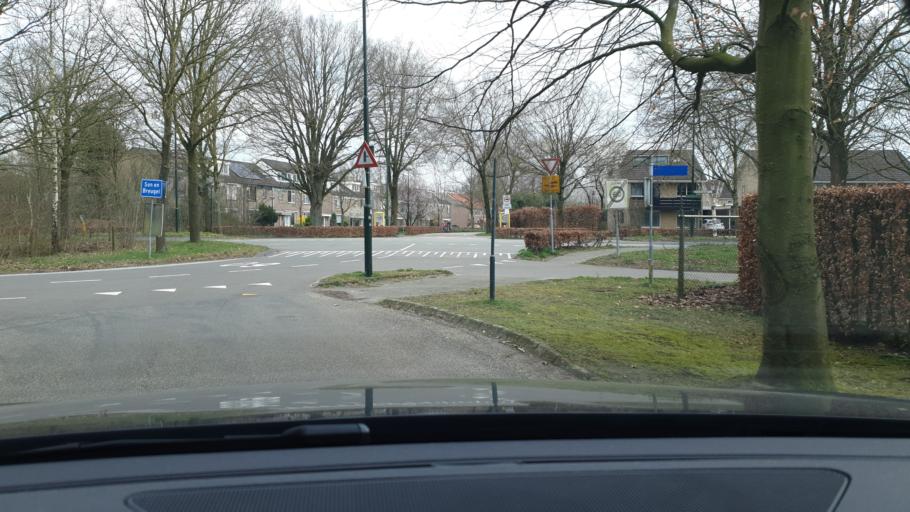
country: NL
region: North Brabant
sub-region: Gemeente Son en Breugel
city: Breugel
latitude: 51.5235
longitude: 5.5112
